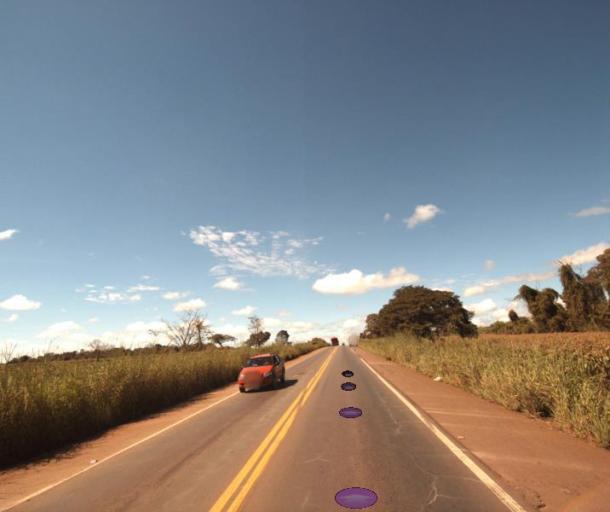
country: BR
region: Goias
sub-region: Rialma
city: Rialma
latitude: -15.3748
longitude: -49.5567
